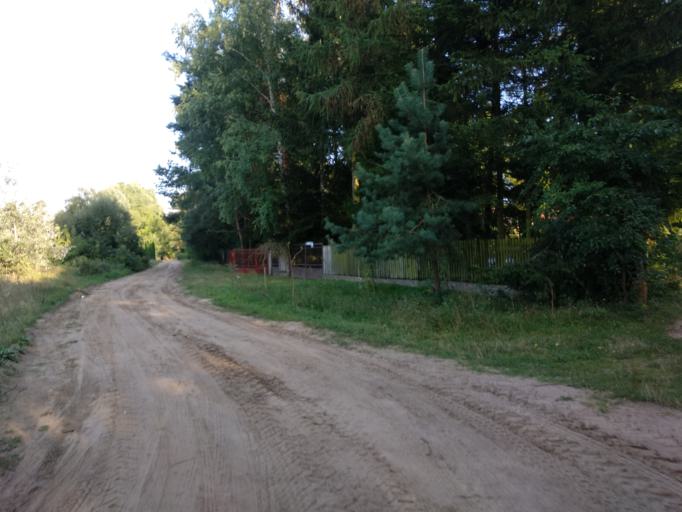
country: PL
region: Masovian Voivodeship
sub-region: Powiat pultuski
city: Obryte
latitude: 52.7577
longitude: 21.1837
